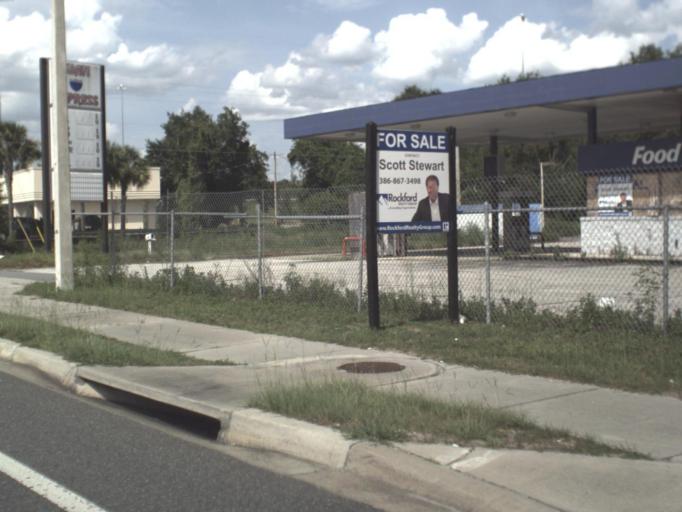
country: US
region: Florida
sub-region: Columbia County
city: Lake City
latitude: 30.1152
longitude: -82.6570
